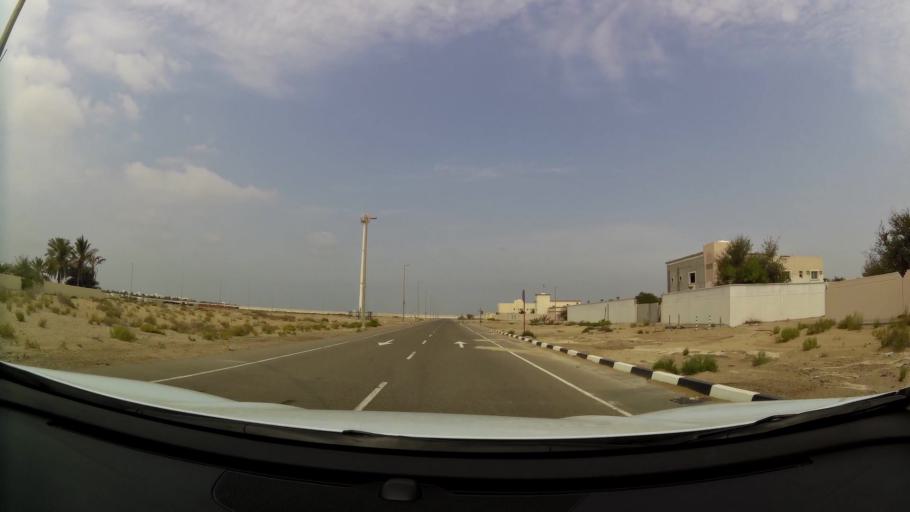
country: AE
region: Abu Dhabi
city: Abu Dhabi
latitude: 24.6289
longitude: 54.6579
